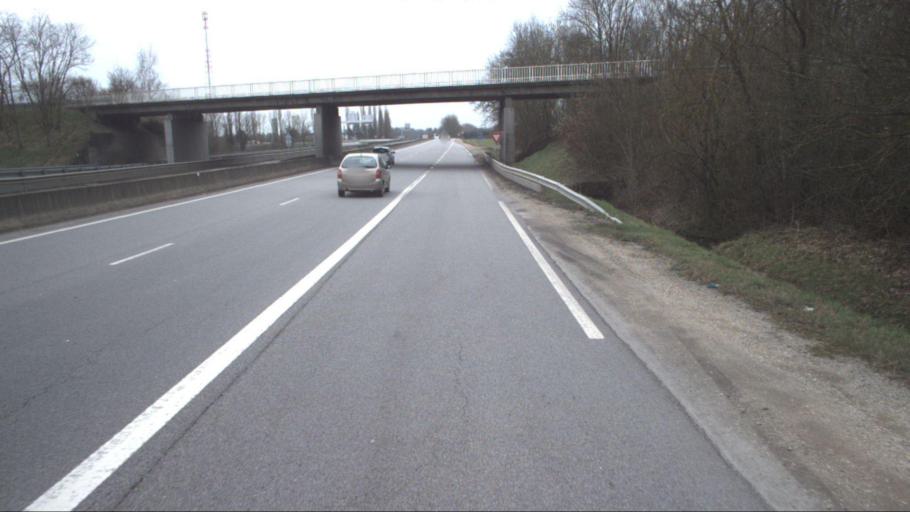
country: FR
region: Ile-de-France
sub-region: Departement des Yvelines
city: Ablis
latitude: 48.5316
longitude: 1.8297
